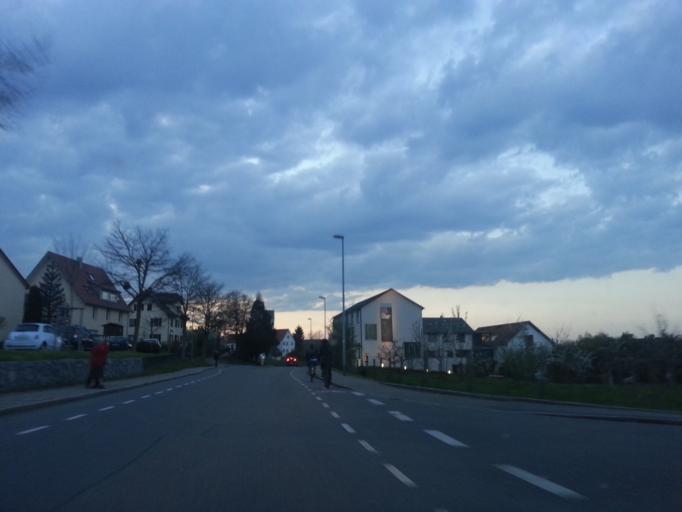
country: DE
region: Baden-Wuerttemberg
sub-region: Tuebingen Region
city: Friedrichshafen
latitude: 47.6697
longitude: 9.4741
